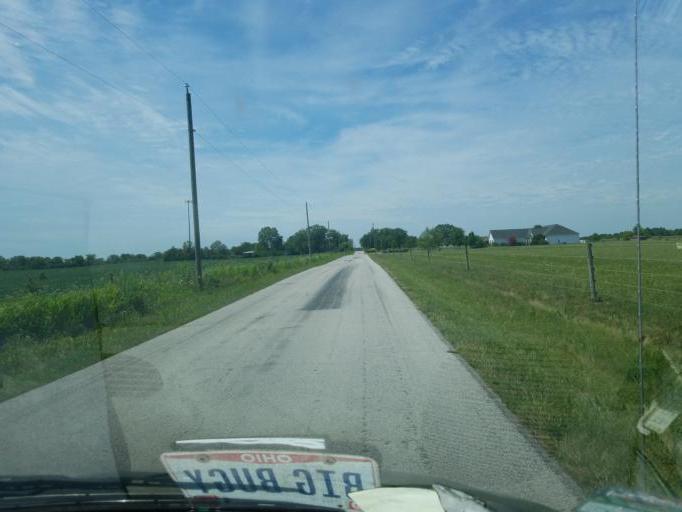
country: US
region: Ohio
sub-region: Franklin County
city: Lake Darby
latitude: 39.8770
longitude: -83.1967
